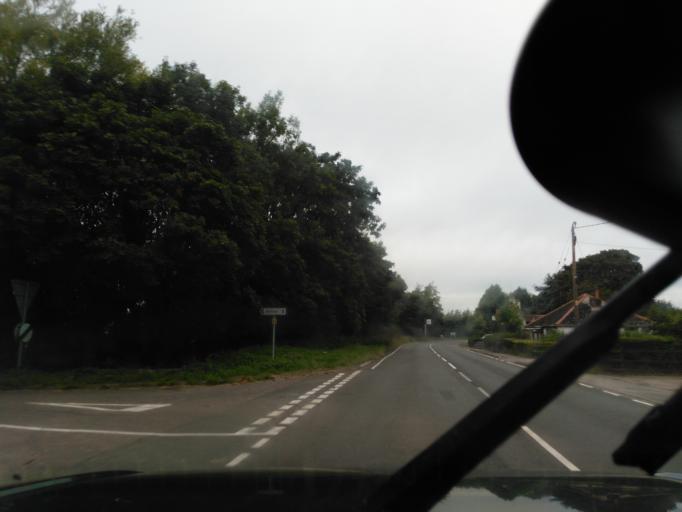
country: GB
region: England
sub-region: Dorset
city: Lytchett Matravers
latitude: 50.7973
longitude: -2.0834
